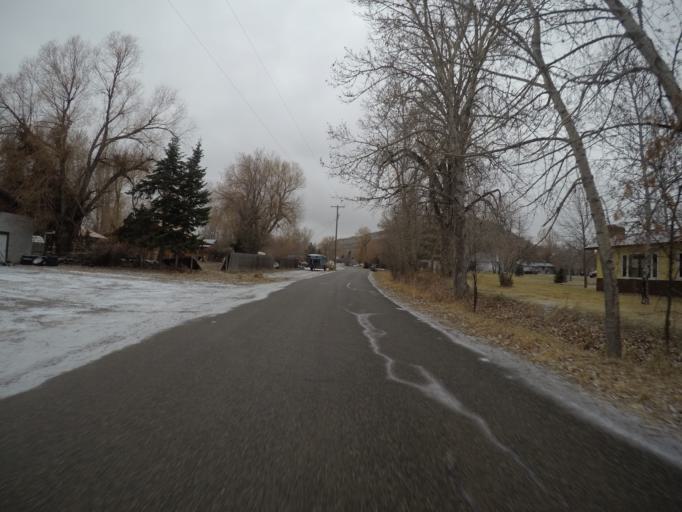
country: US
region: Montana
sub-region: Stillwater County
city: Absarokee
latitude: 45.5240
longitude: -109.4441
